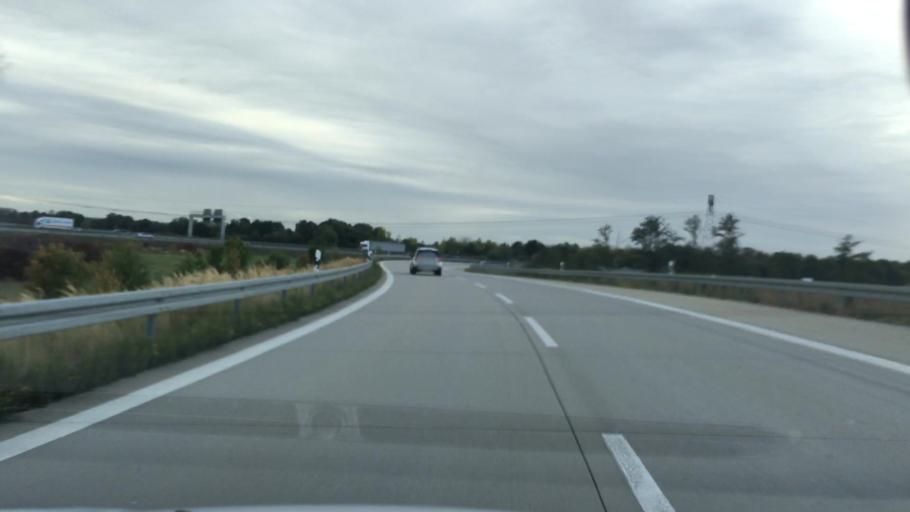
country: DE
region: Saxony
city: Borsdorf
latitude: 51.3135
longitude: 12.5473
